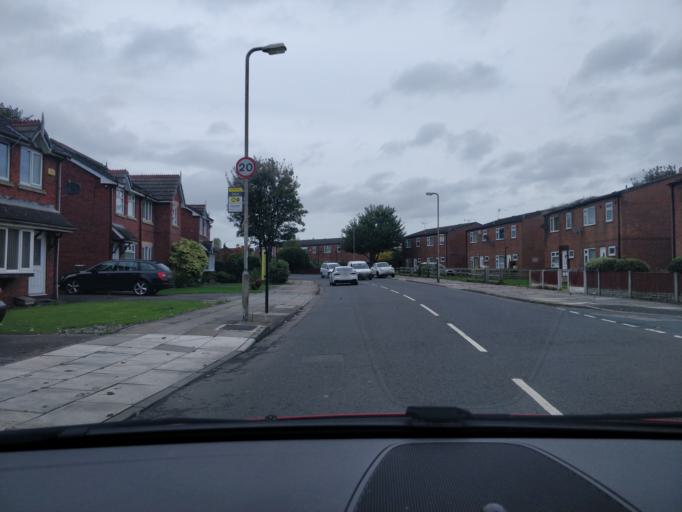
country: GB
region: England
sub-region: Sefton
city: Southport
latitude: 53.6337
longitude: -2.9863
